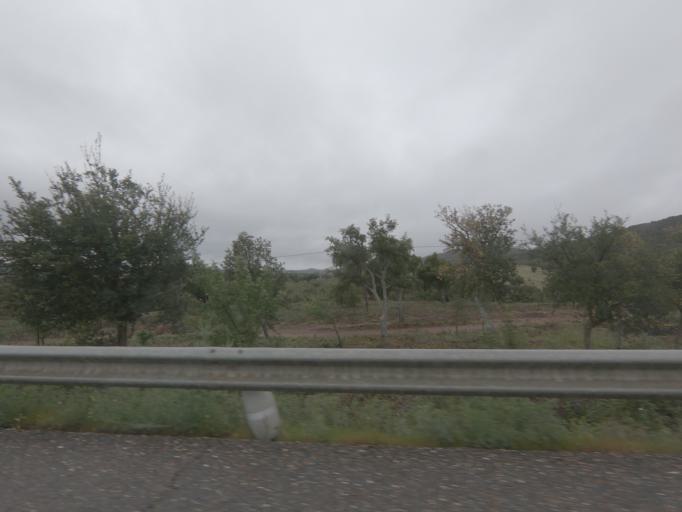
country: ES
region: Extremadura
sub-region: Provincia de Badajoz
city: Puebla de Obando
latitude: 39.1610
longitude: -6.6416
